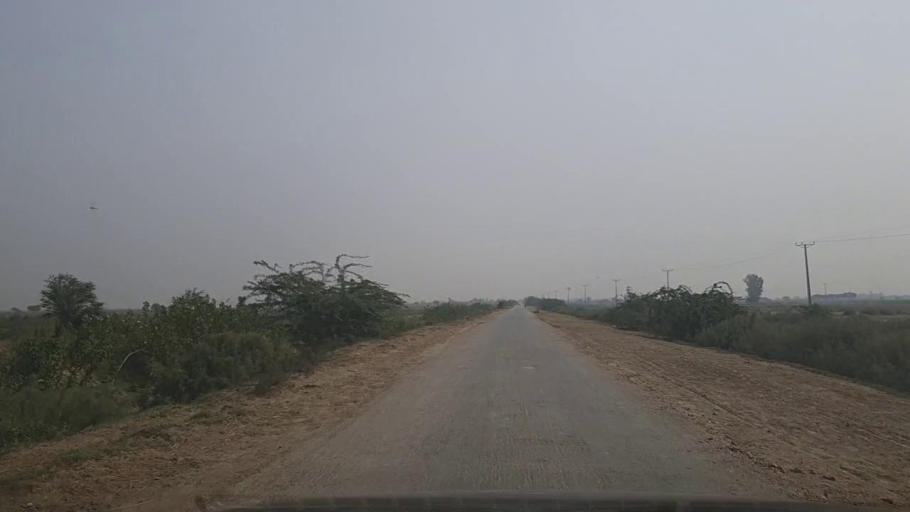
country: PK
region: Sindh
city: Mirpur Sakro
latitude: 24.4780
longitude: 67.6604
